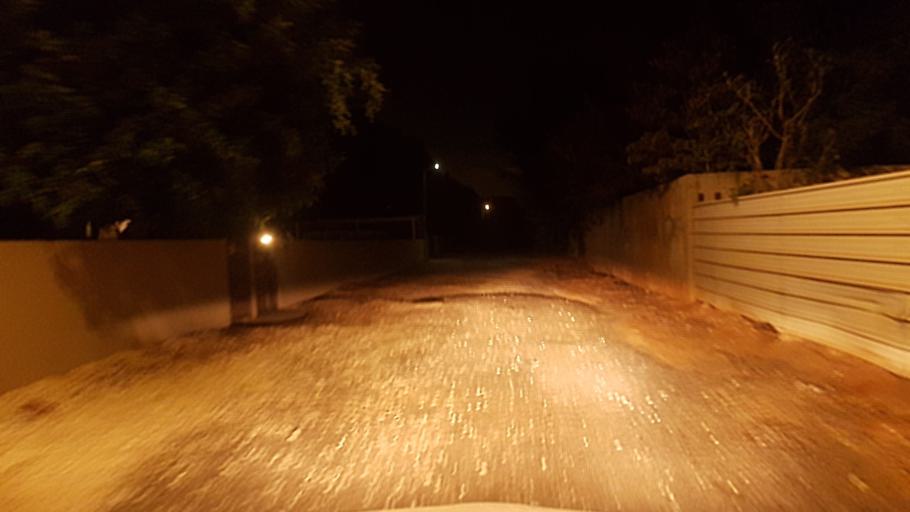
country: IL
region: Central District
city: Hod HaSharon
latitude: 32.1588
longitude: 34.8736
